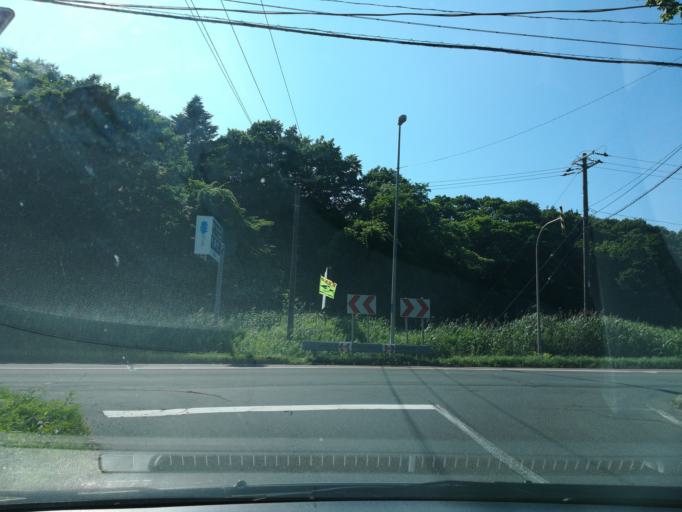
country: JP
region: Hokkaido
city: Chitose
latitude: 42.9116
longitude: 141.7270
